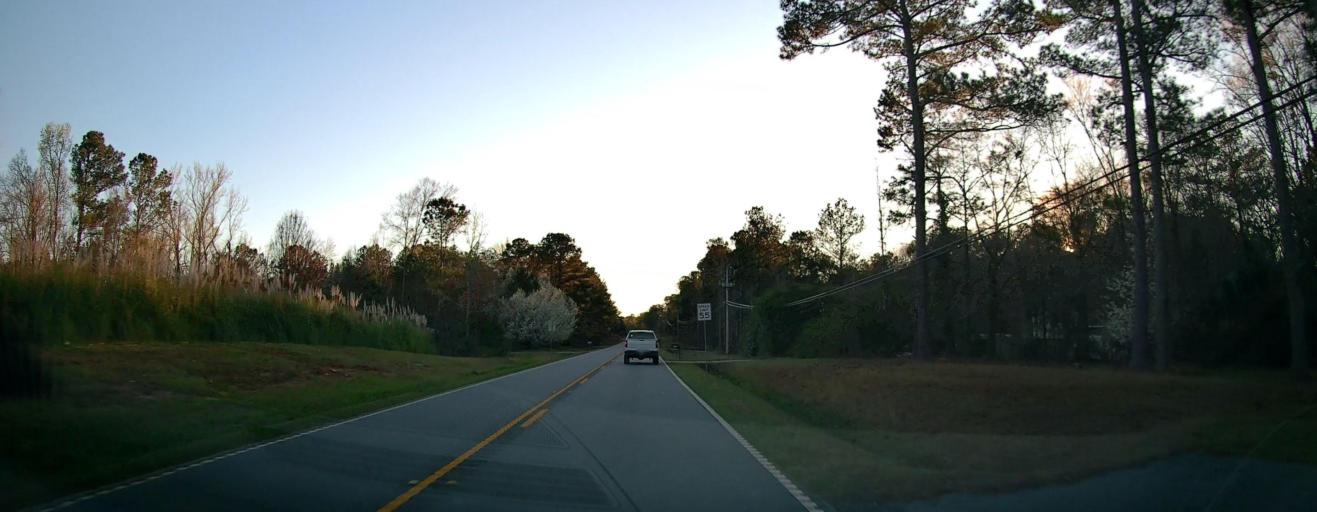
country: US
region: Alabama
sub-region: Lee County
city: Smiths Station
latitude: 32.6484
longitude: -85.0148
